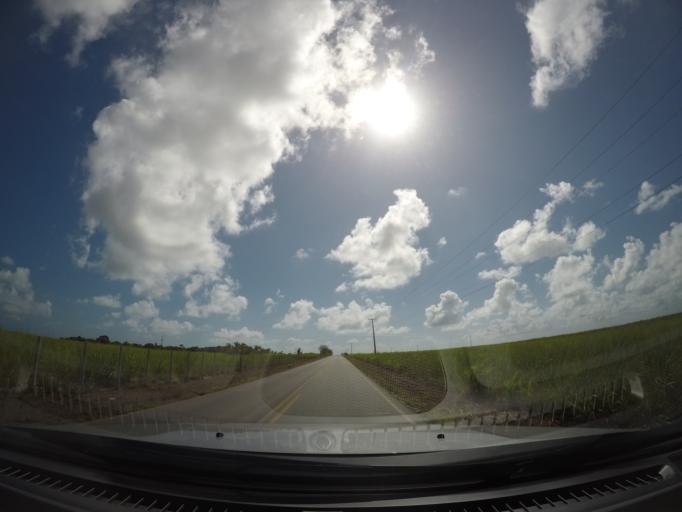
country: BR
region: Paraiba
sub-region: Pitimbu
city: Pitimbu
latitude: -7.4714
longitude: -34.8287
